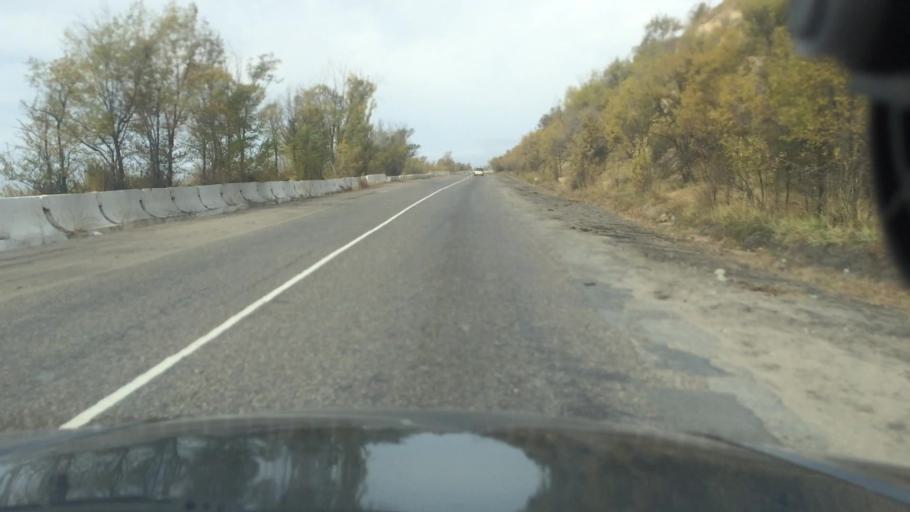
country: KG
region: Ysyk-Koel
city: Karakol
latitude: 42.5958
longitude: 78.3813
